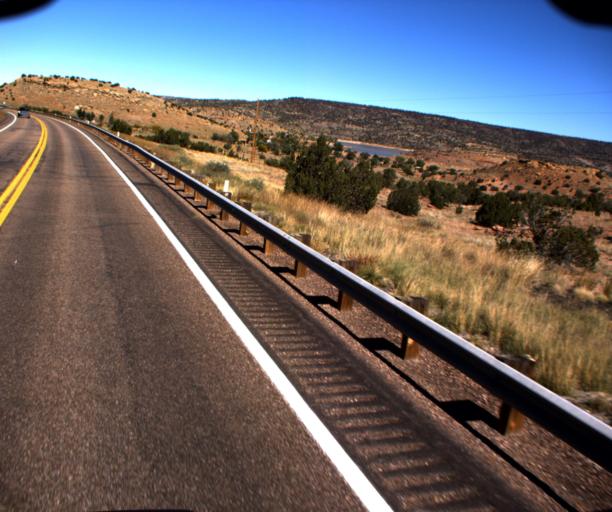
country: US
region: Arizona
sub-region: Apache County
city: Saint Johns
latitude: 34.3522
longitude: -109.3785
